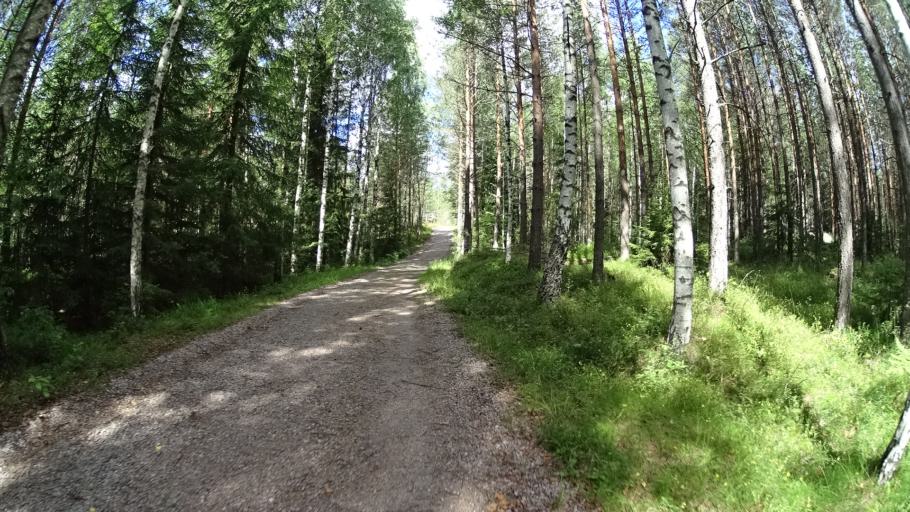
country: FI
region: Uusimaa
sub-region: Helsinki
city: Espoo
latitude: 60.2668
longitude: 24.6242
